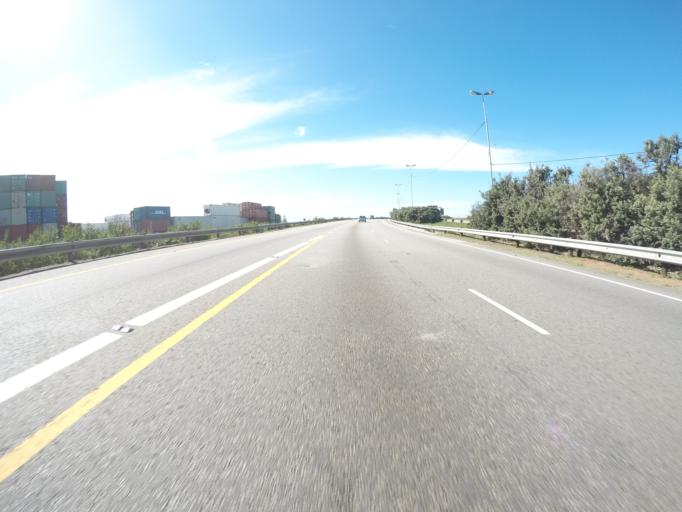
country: ZA
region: Eastern Cape
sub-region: Nelson Mandela Bay Metropolitan Municipality
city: Port Elizabeth
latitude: -33.9136
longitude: 25.6028
